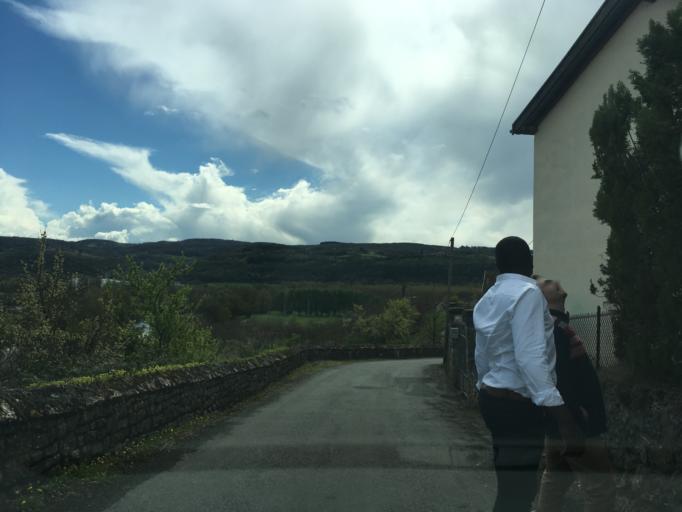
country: FR
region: Midi-Pyrenees
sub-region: Departement de l'Aveyron
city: Capdenac-Gare
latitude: 44.5746
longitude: 2.0694
